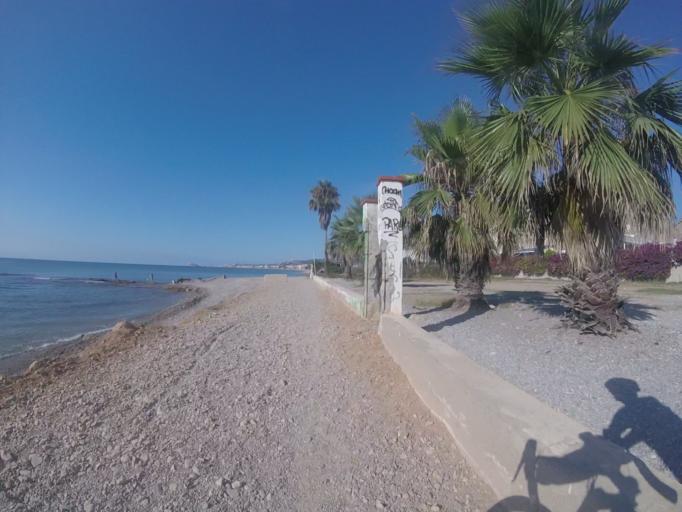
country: ES
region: Valencia
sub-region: Provincia de Castello
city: Benicarlo
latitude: 40.4088
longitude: 0.4263
